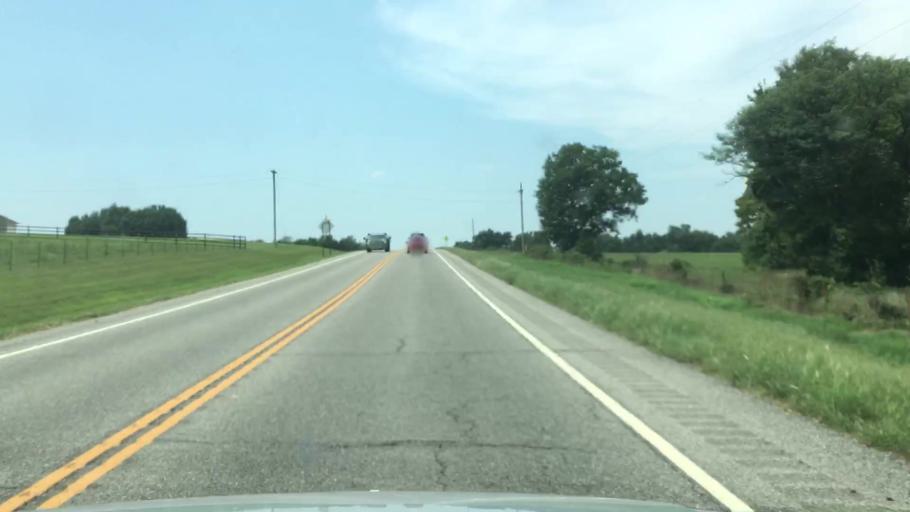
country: US
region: Oklahoma
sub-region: Muskogee County
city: Fort Gibson
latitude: 35.9369
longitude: -95.1913
